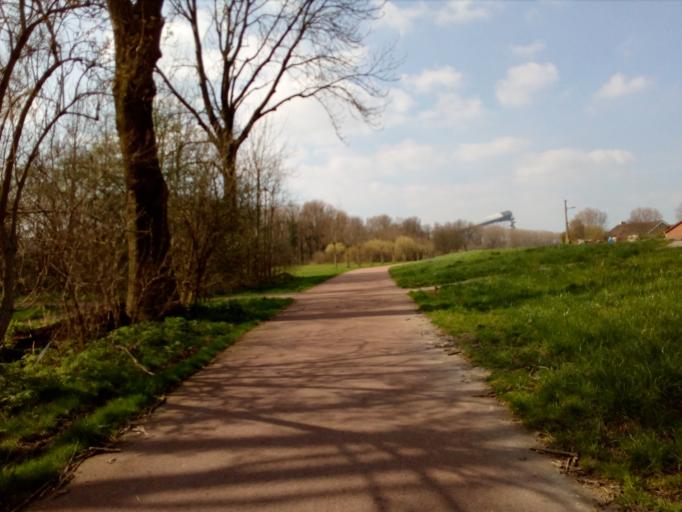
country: NL
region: South Holland
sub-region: Gemeente Zoetermeer
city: Zoetermeer
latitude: 52.0703
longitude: 4.4705
